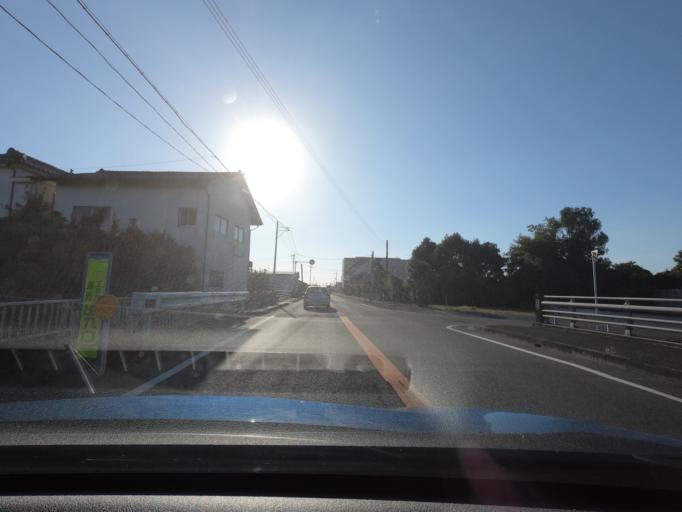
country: JP
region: Kagoshima
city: Izumi
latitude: 32.0985
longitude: 130.3050
